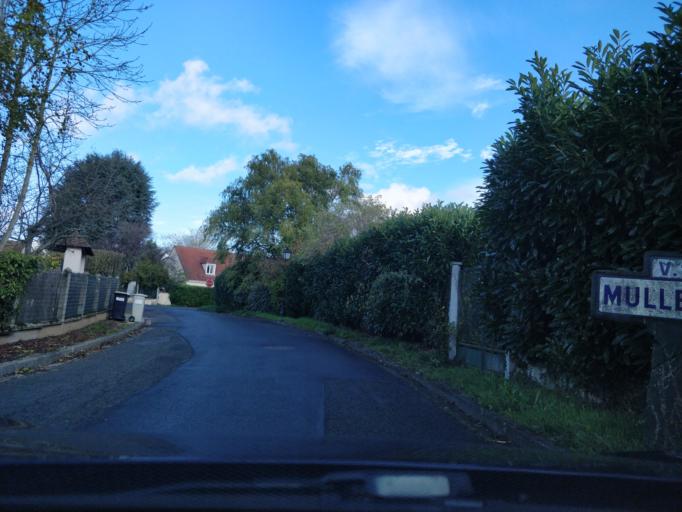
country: FR
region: Ile-de-France
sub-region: Departement de l'Essonne
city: Fontenay-les-Briis
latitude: 48.6340
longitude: 2.1590
